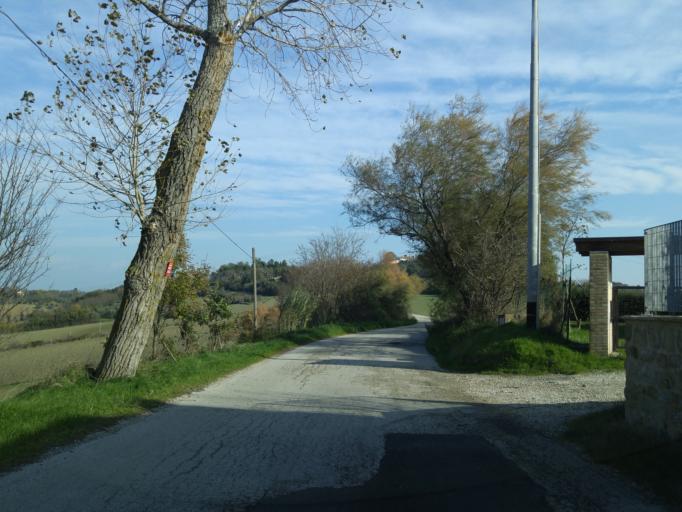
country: IT
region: The Marches
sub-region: Provincia di Pesaro e Urbino
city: Cuccurano
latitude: 43.8190
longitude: 12.9187
